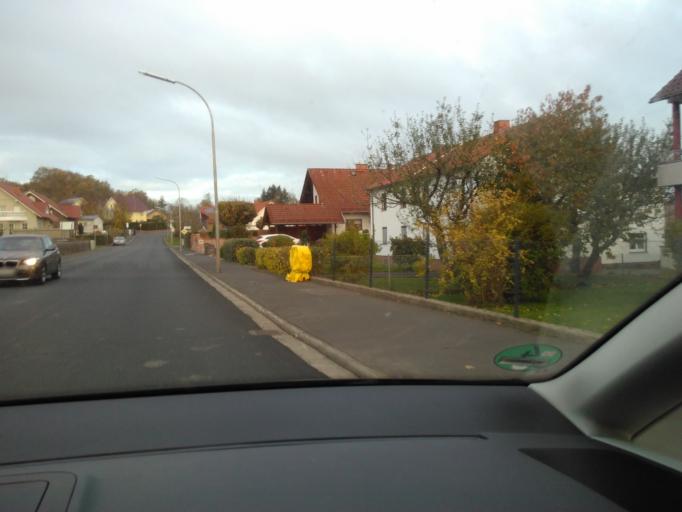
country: DE
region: Hesse
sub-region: Regierungsbezirk Giessen
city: Lauterbach
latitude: 50.6413
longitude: 9.3864
